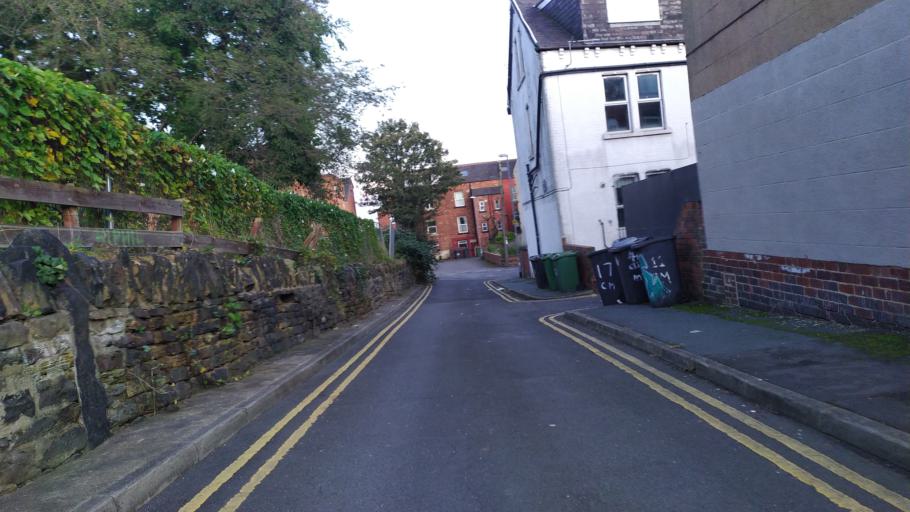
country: GB
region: England
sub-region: City and Borough of Leeds
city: Leeds
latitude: 53.8170
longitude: -1.5577
